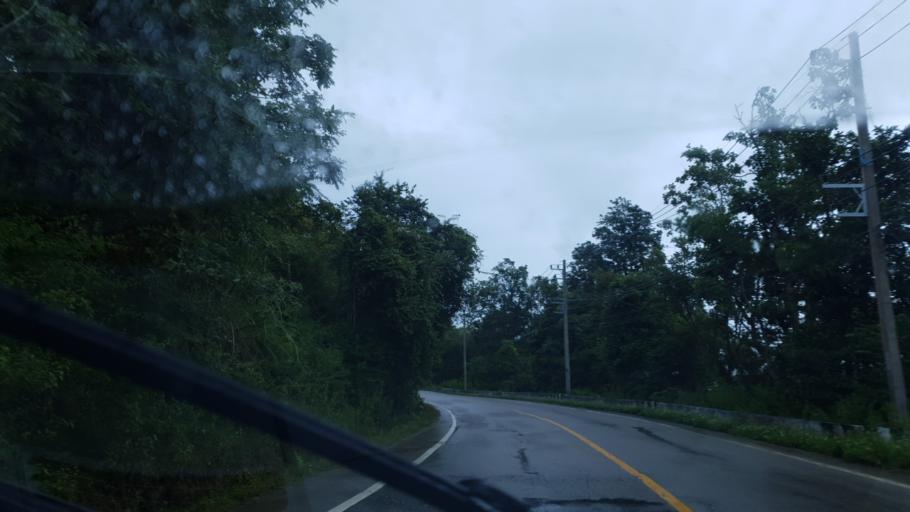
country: TH
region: Mae Hong Son
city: Ban Huai I Huak
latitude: 18.1340
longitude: 98.1802
